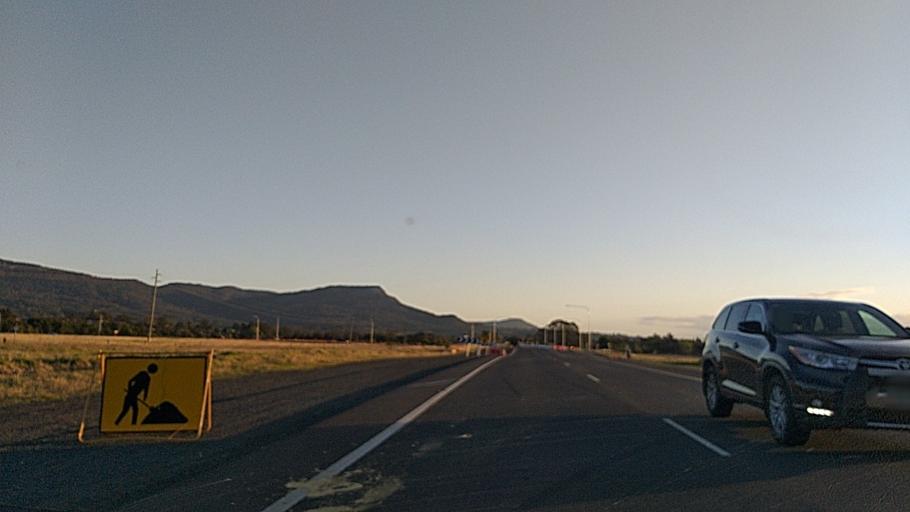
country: AU
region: New South Wales
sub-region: Wollongong
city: Dapto
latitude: -34.5014
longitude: 150.7790
